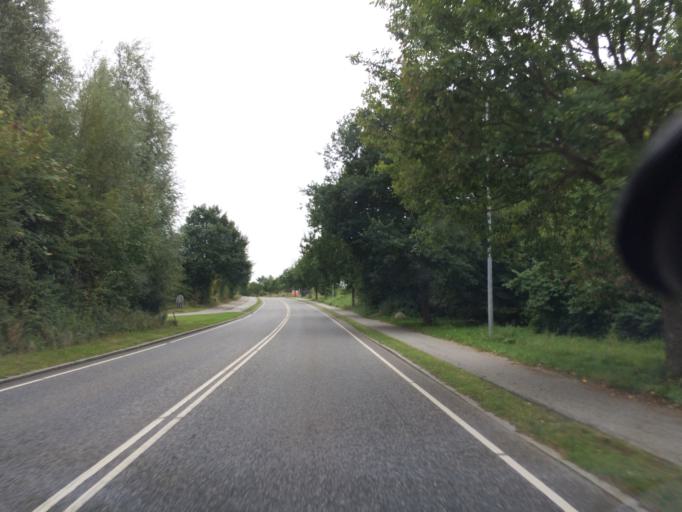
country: DK
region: South Denmark
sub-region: Aabenraa Kommune
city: Aabenraa
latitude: 55.0268
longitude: 9.4099
